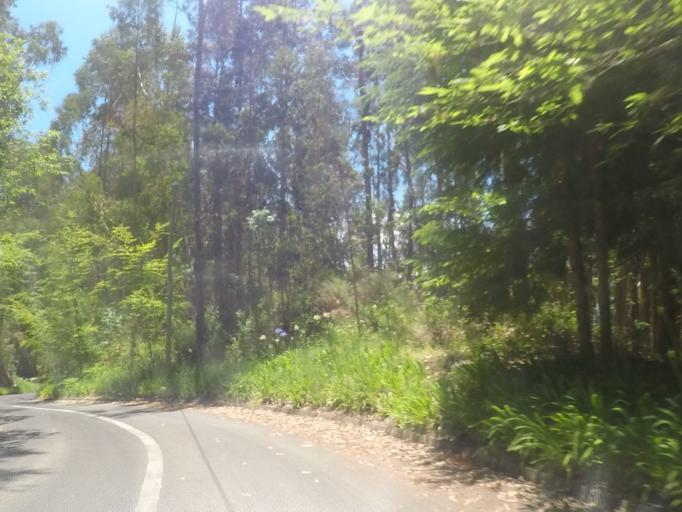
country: PT
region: Madeira
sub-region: Camara de Lobos
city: Curral das Freiras
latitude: 32.6939
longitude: -16.9782
